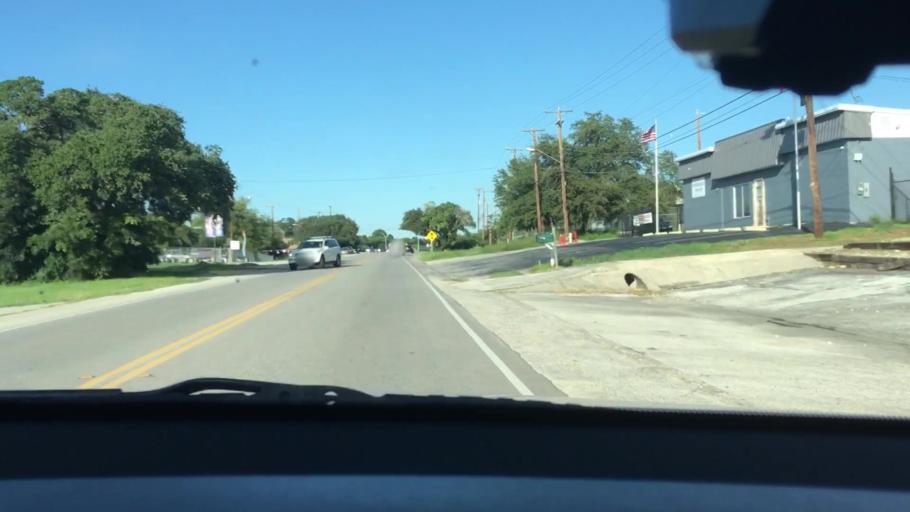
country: US
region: Texas
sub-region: Bexar County
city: Live Oak
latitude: 29.5497
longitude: -98.3581
